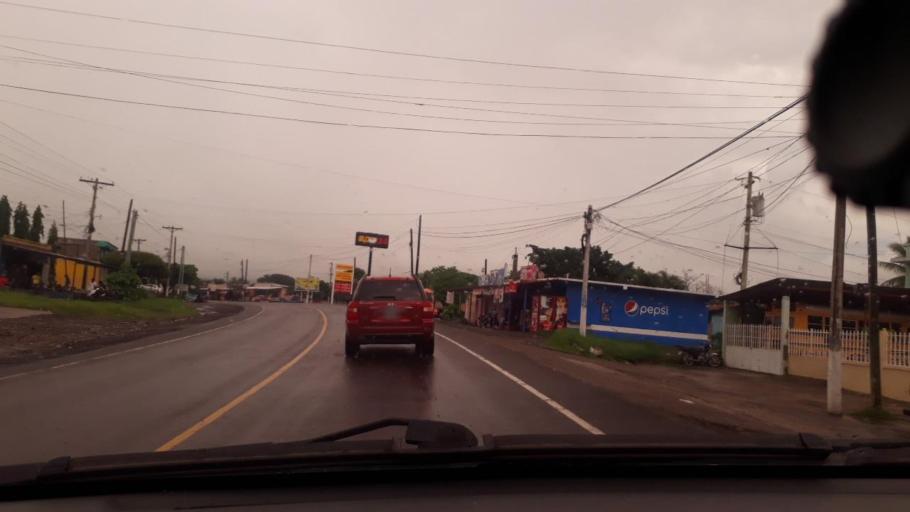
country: SV
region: Ahuachapan
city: San Francisco Menendez
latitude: 13.8783
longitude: -90.0969
